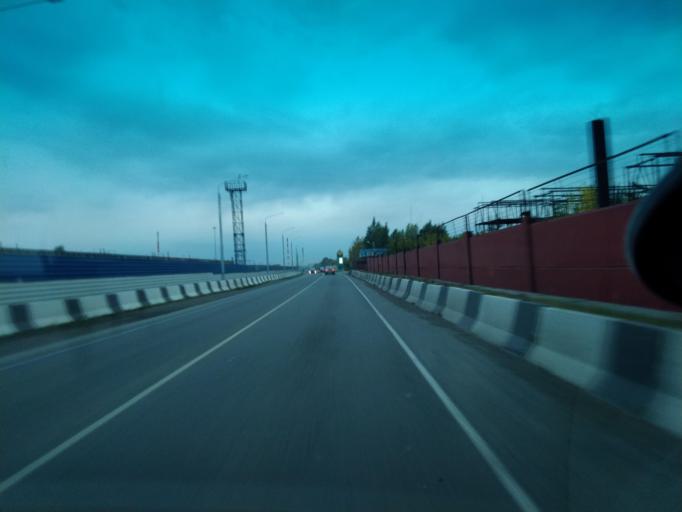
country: RU
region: Krasnoyarskiy
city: Berezovka
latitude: 56.0241
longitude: 93.0974
